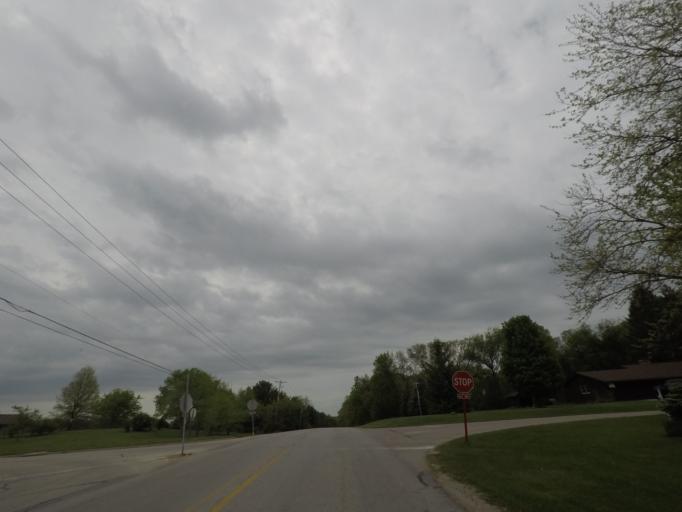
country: US
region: Illinois
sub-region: Winnebago County
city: Roscoe
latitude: 42.4252
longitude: -88.9752
